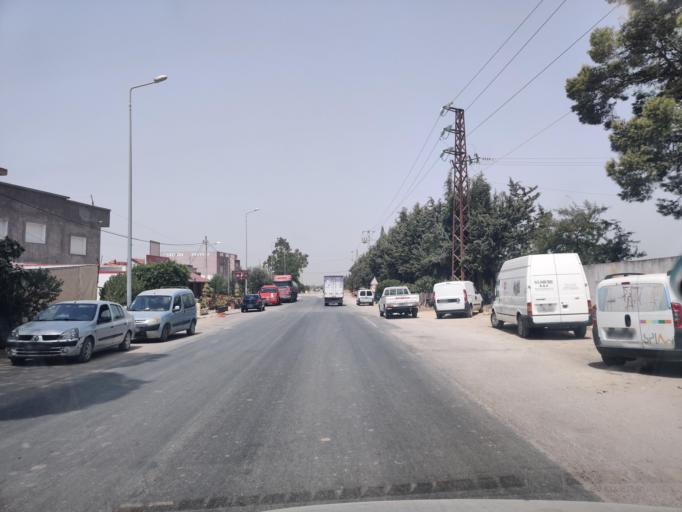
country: TN
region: Tunis
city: La Sebala du Mornag
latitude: 36.6621
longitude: 10.3237
